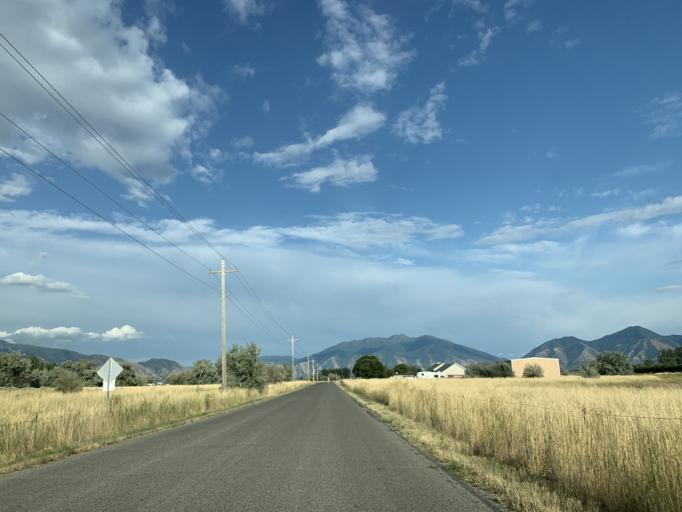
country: US
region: Utah
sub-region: Utah County
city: Benjamin
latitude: 40.1164
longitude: -111.7733
